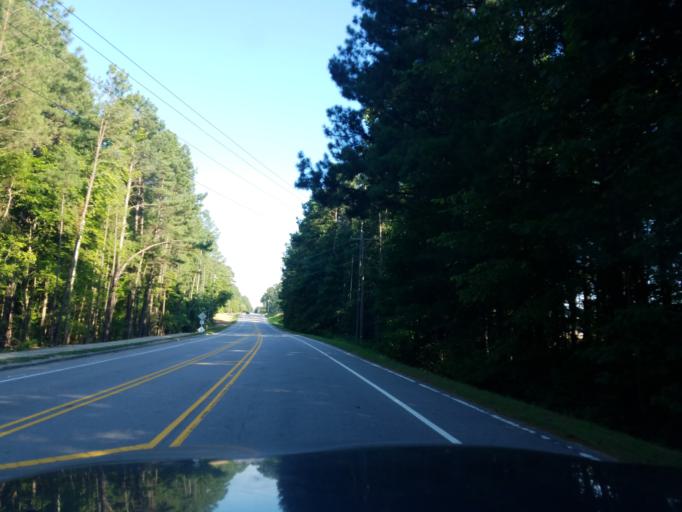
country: US
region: North Carolina
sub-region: Orange County
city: Chapel Hill
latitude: 35.8825
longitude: -78.9557
